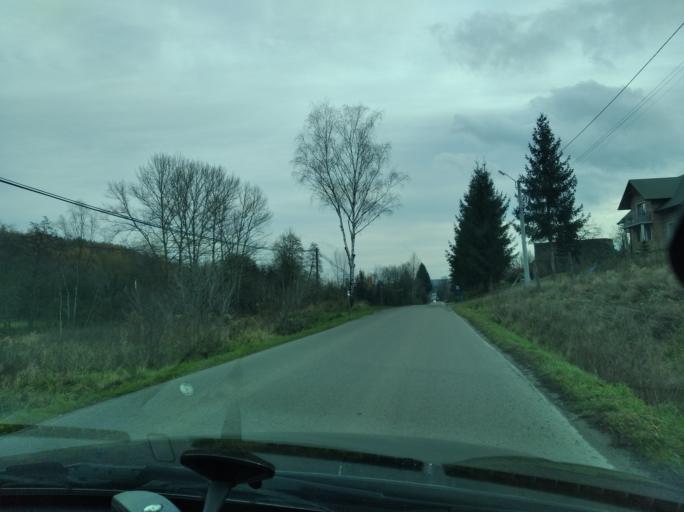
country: PL
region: Subcarpathian Voivodeship
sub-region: Powiat strzyzowski
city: Strzyzow
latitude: 49.9406
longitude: 21.7545
